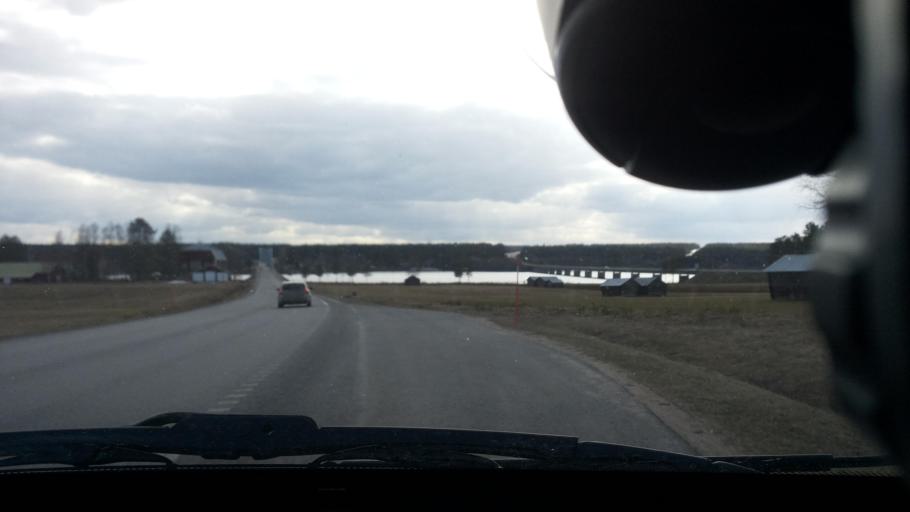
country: SE
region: Norrbotten
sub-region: Lulea Kommun
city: Gammelstad
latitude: 65.5936
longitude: 22.0434
